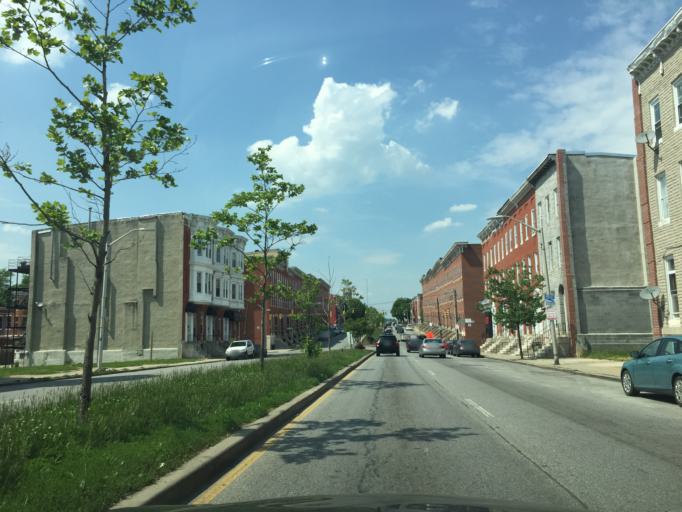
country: US
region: Maryland
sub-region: City of Baltimore
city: Baltimore
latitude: 39.2980
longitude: -76.6456
